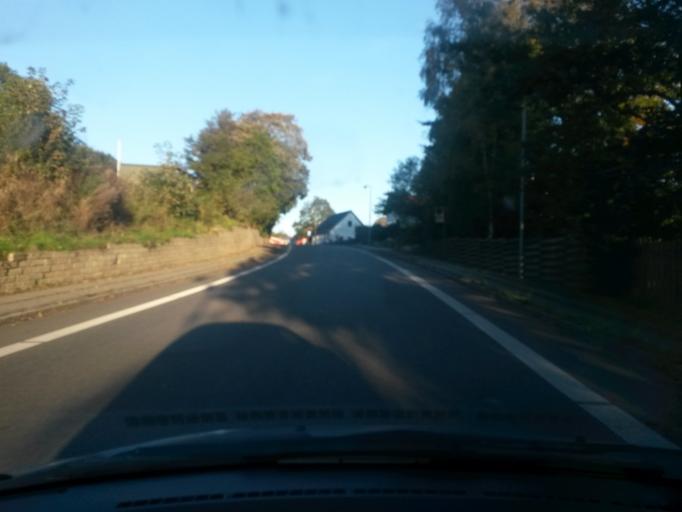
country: DK
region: Central Jutland
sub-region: Silkeborg Kommune
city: Kjellerup
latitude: 56.2860
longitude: 9.3276
